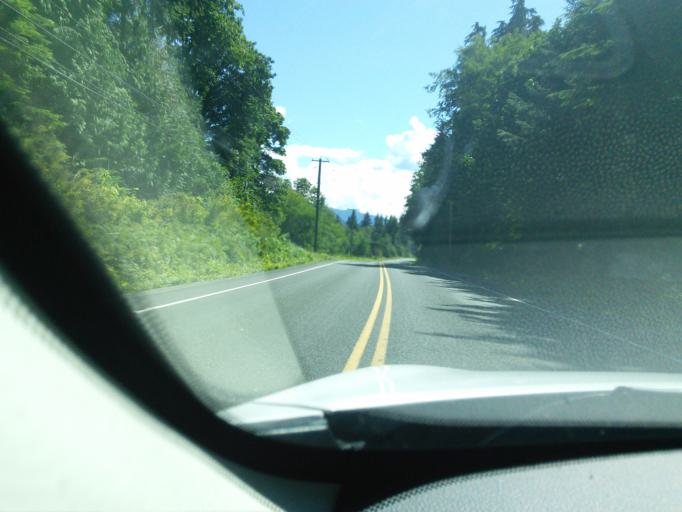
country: CA
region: British Columbia
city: Campbell River
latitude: 50.3321
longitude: -125.9197
